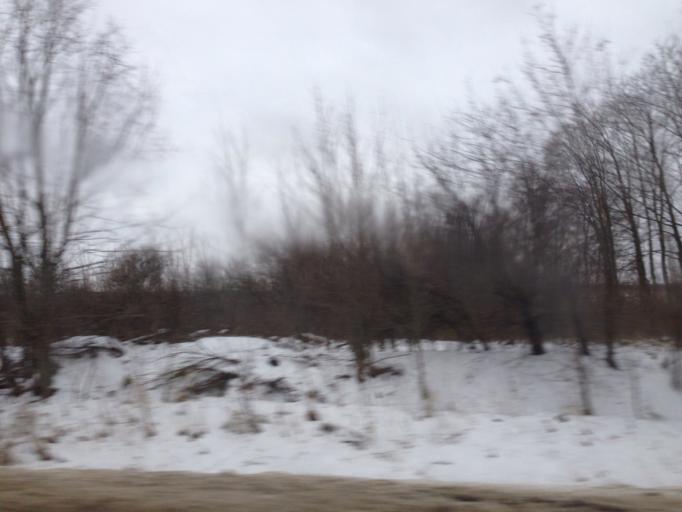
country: RU
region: Tula
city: Kamenetskiy
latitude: 53.9944
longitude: 38.2108
